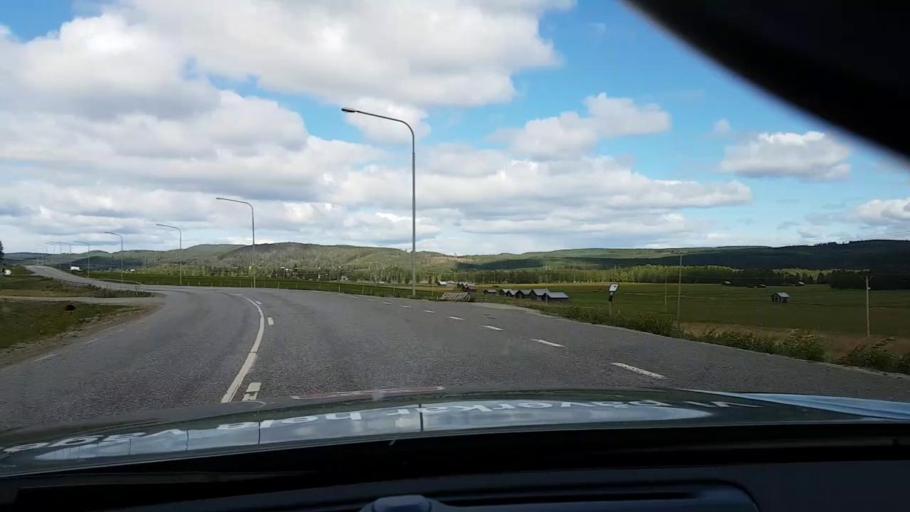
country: SE
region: Vaesternorrland
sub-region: OErnskoeldsviks Kommun
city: Bredbyn
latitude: 63.4977
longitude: 18.0830
